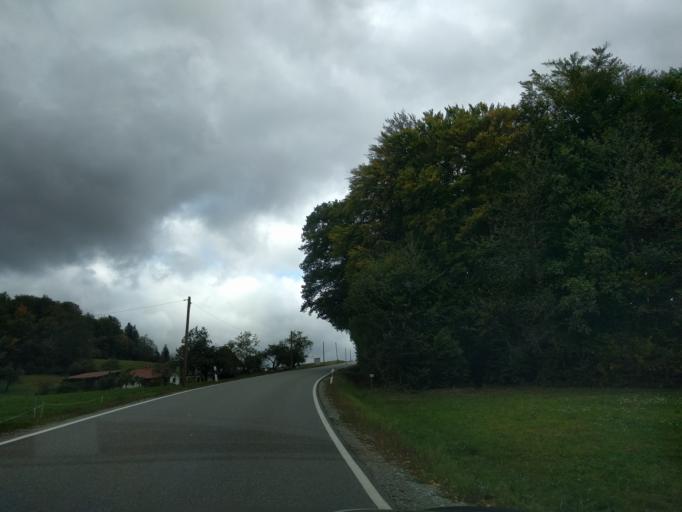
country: DE
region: Bavaria
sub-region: Lower Bavaria
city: Schaufling
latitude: 48.8338
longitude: 13.0517
